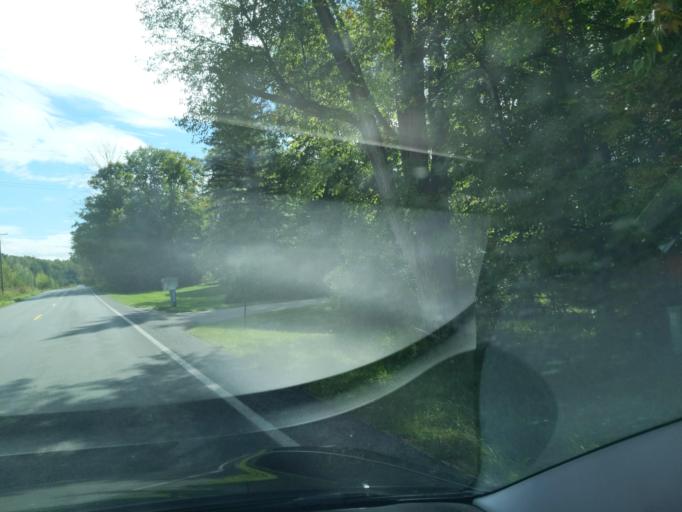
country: US
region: Michigan
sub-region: Antrim County
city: Bellaire
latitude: 45.0156
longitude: -85.2921
